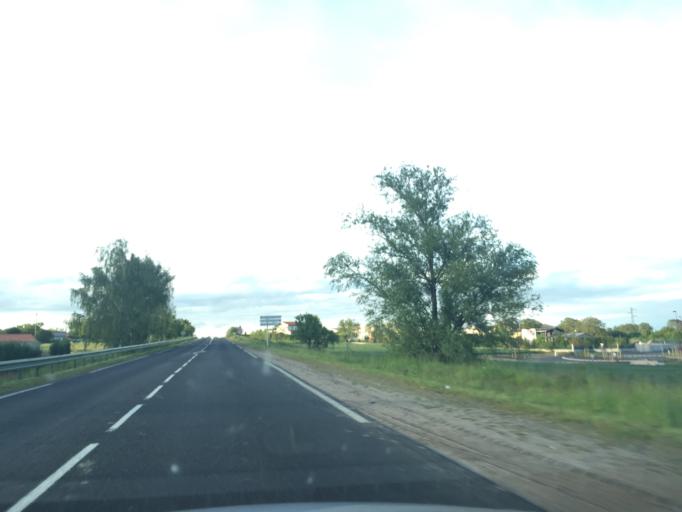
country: FR
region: Auvergne
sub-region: Departement du Puy-de-Dome
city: Chatel-Guyon
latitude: 45.9173
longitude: 3.0832
